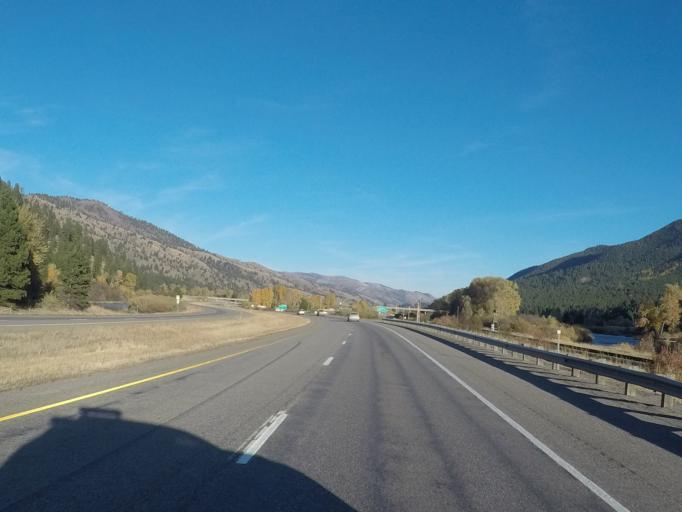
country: US
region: Montana
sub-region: Missoula County
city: Clinton
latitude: 46.7258
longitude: -113.6815
